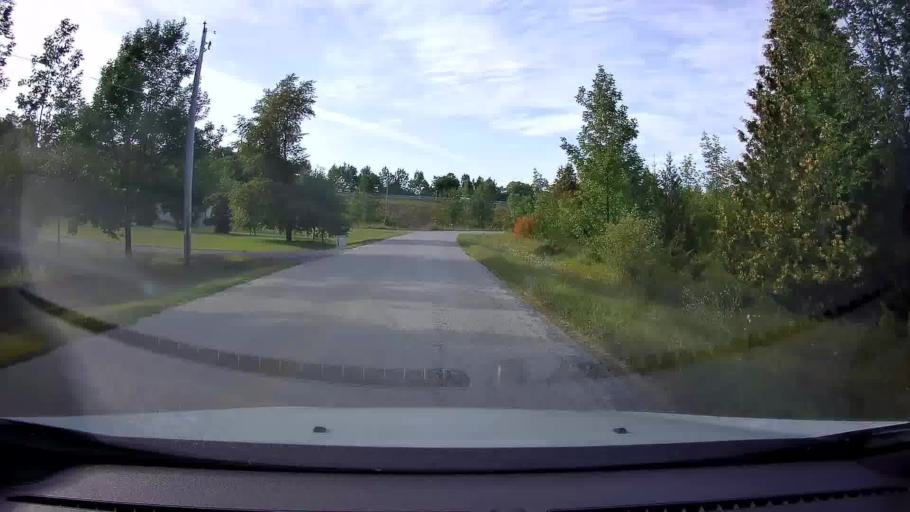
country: US
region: Wisconsin
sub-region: Door County
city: Sturgeon Bay
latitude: 45.1801
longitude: -87.1457
